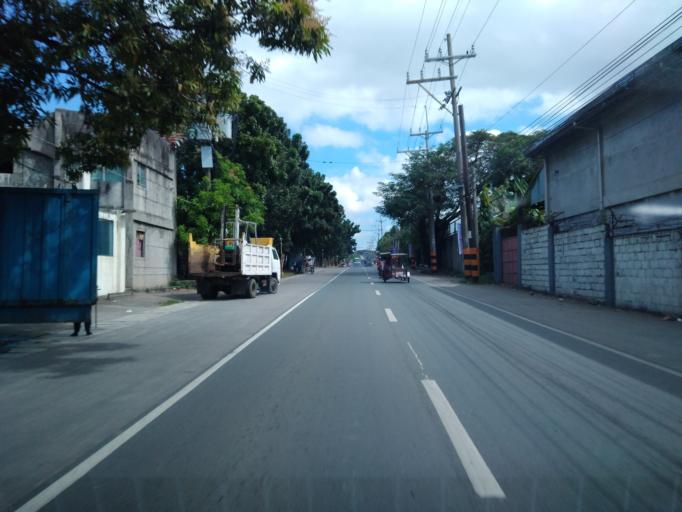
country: PH
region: Central Luzon
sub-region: Province of Bulacan
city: Guyong
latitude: 14.8303
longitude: 120.9728
